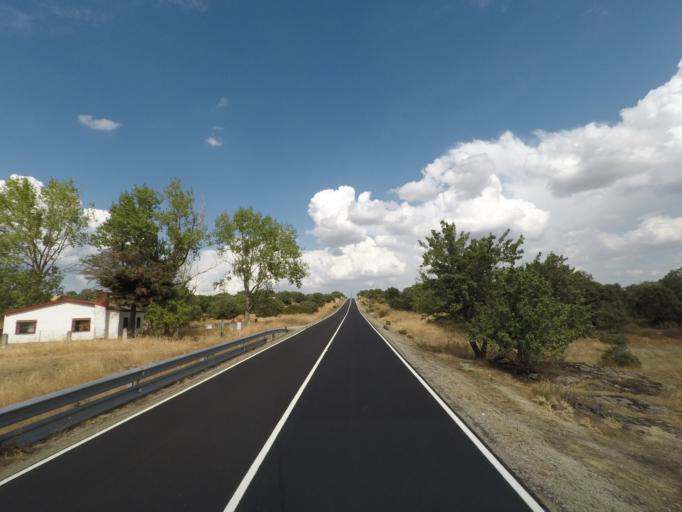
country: ES
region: Castille and Leon
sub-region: Provincia de Salamanca
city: Almendra
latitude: 41.2961
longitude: -6.3307
